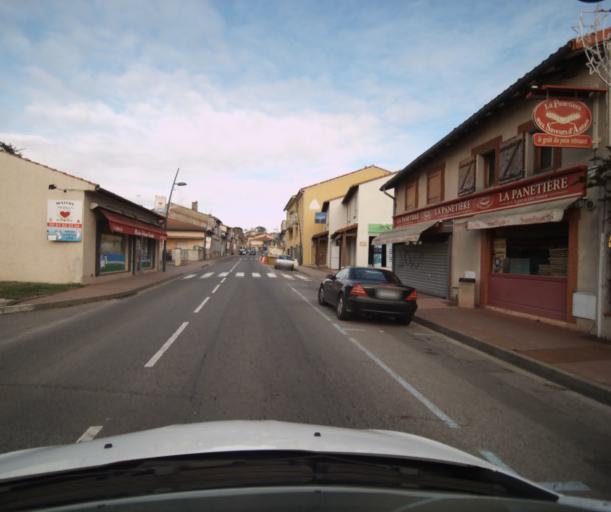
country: FR
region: Midi-Pyrenees
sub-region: Departement de la Haute-Garonne
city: Bruguieres
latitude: 43.7249
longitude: 1.4107
